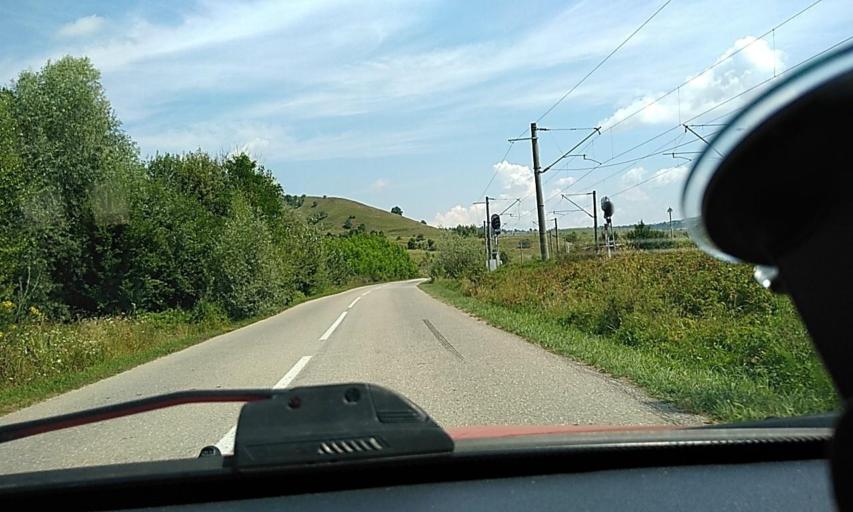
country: RO
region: Brasov
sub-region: Comuna Hoghiz
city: Hoghiz
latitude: 46.0289
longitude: 25.3618
